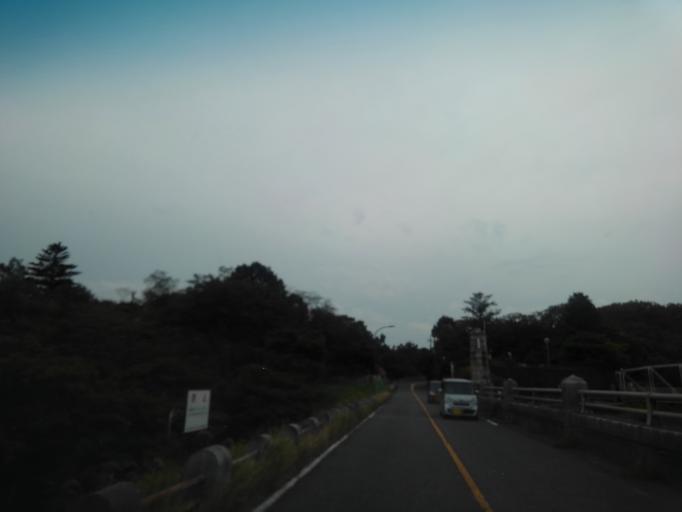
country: JP
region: Tokyo
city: Higashimurayama-shi
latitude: 35.7623
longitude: 139.4171
